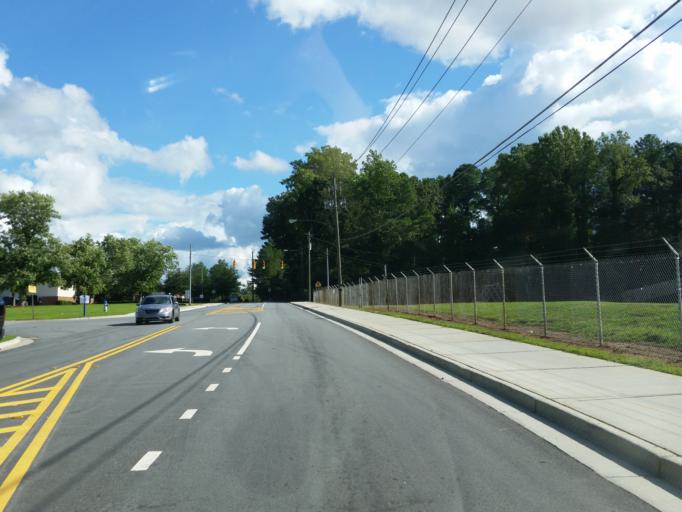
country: US
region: Georgia
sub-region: Cobb County
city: Smyrna
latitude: 33.8907
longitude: -84.5274
